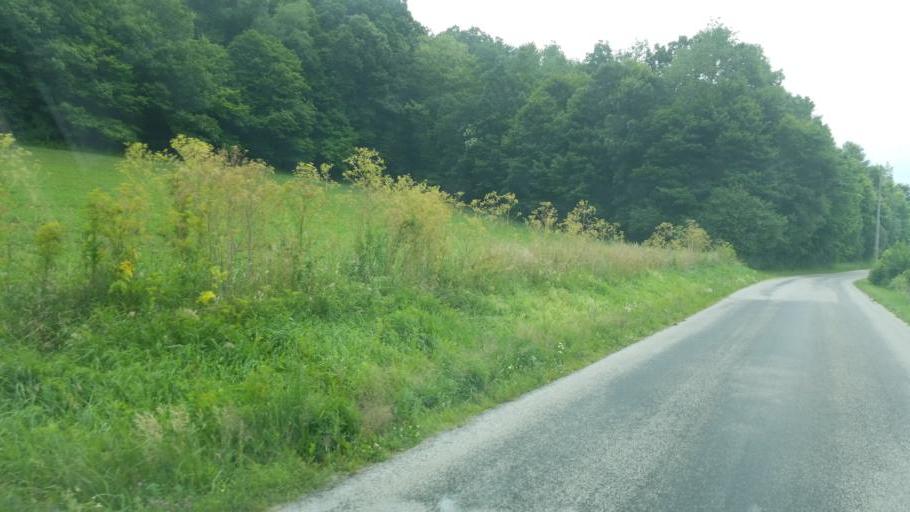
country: US
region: Ohio
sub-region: Licking County
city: Utica
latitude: 40.1692
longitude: -82.4293
